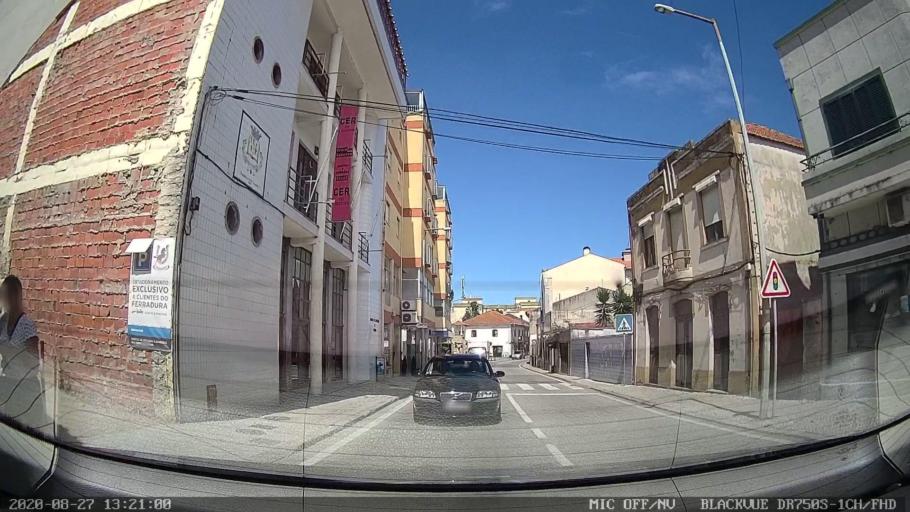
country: PT
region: Aveiro
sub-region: Vagos
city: Vagos
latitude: 40.5542
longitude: -8.6813
